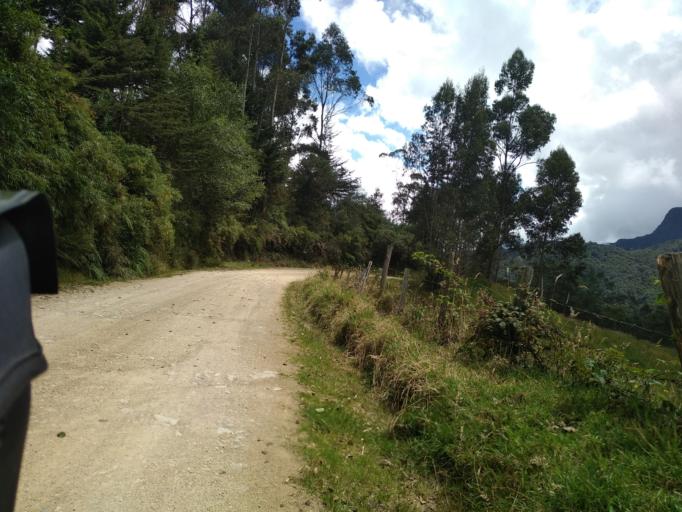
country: CO
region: Boyaca
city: Duitama
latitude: 5.9430
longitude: -73.1300
